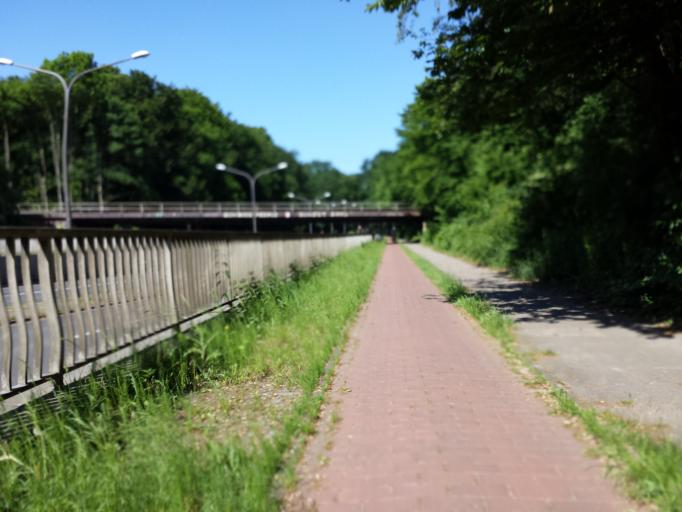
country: DE
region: Bremen
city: Bremen
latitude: 53.1009
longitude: 8.8382
